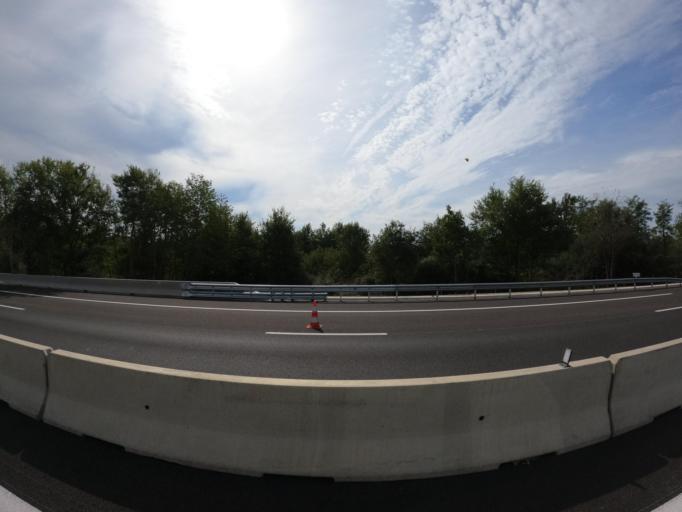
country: FR
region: Auvergne
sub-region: Departement de l'Allier
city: Beaulon
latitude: 46.5345
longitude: 3.5935
